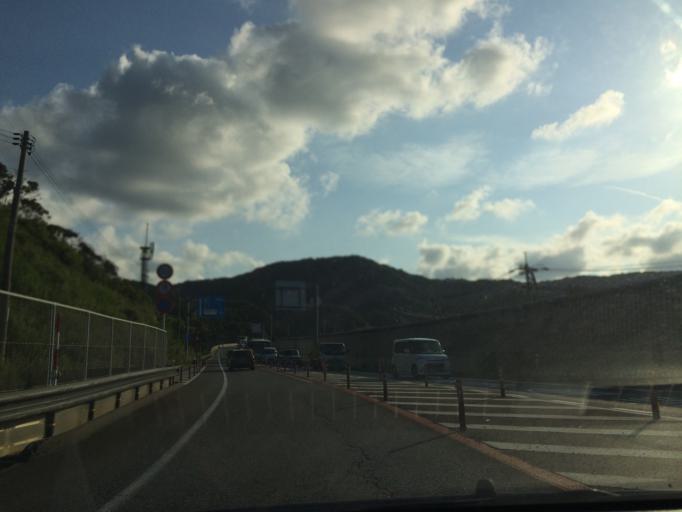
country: JP
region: Tottori
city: Tottori
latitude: 35.5183
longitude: 134.0253
